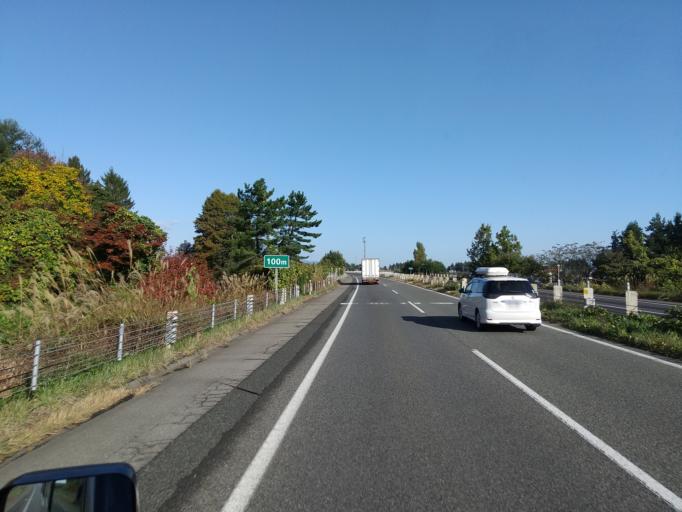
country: JP
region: Iwate
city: Hanamaki
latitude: 39.3372
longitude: 141.0914
